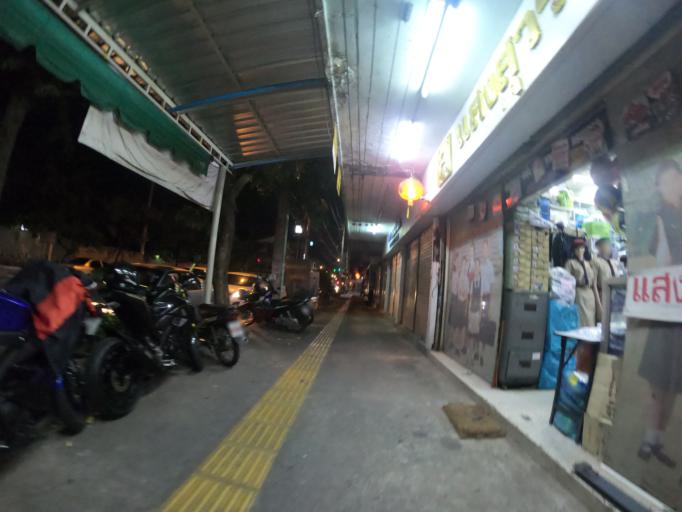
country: TH
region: Khon Kaen
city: Khon Kaen
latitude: 16.4304
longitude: 102.8349
